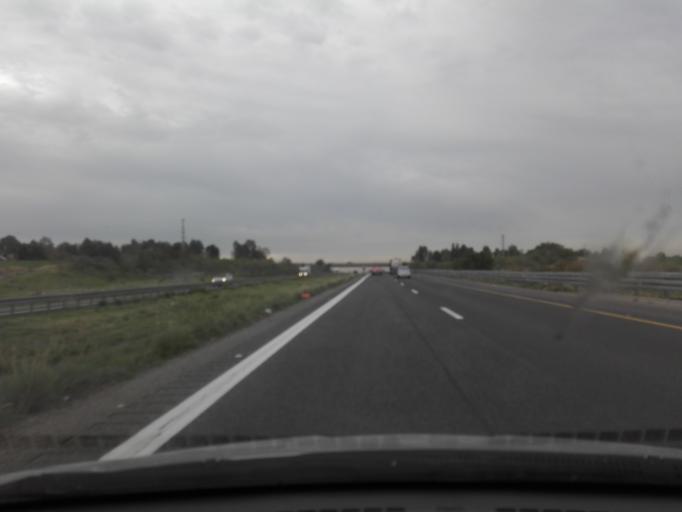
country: IL
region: Central District
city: Mazkeret Batya
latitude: 31.8418
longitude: 34.8627
